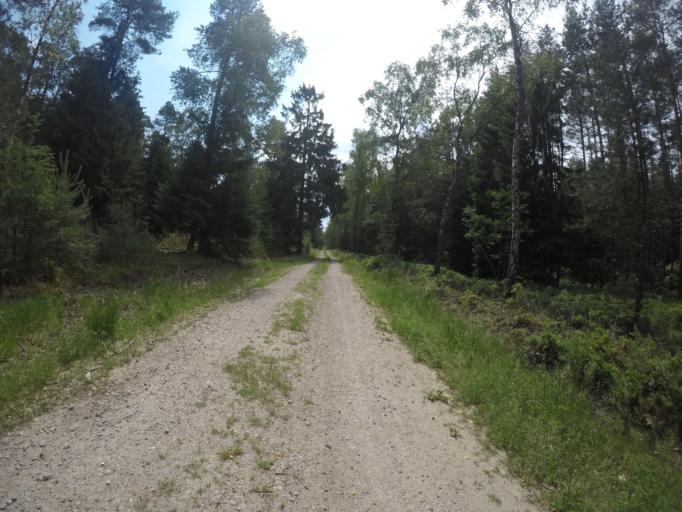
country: DE
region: Lower Saxony
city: Jesteburg
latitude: 53.2587
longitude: 9.9333
